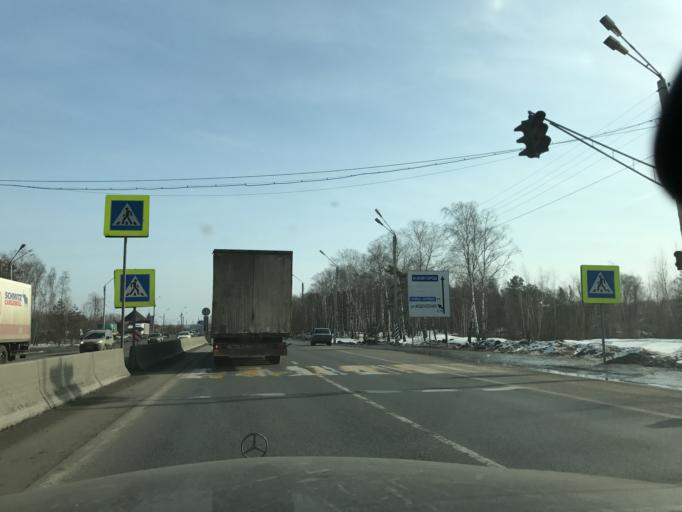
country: RU
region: Nizjnij Novgorod
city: Gorbatovka
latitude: 56.3087
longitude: 43.7424
